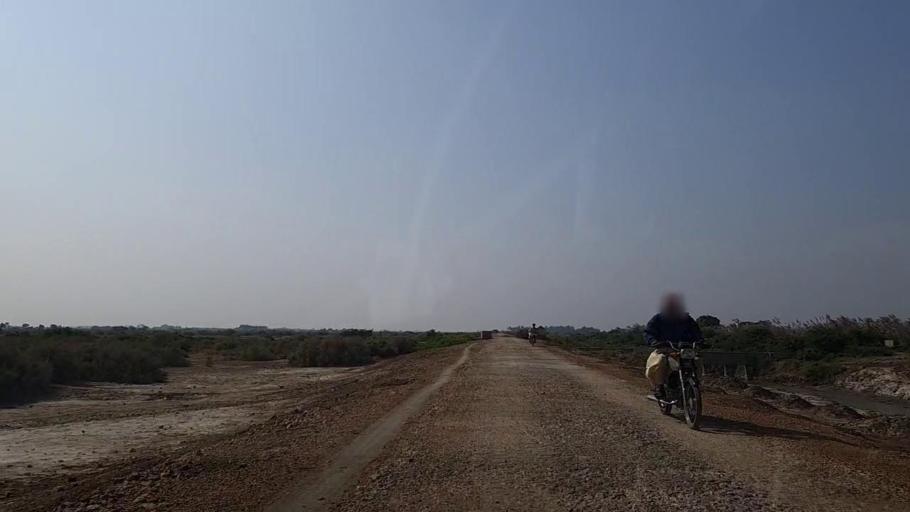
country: PK
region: Sindh
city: Mirpur Sakro
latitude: 24.6347
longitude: 67.7079
